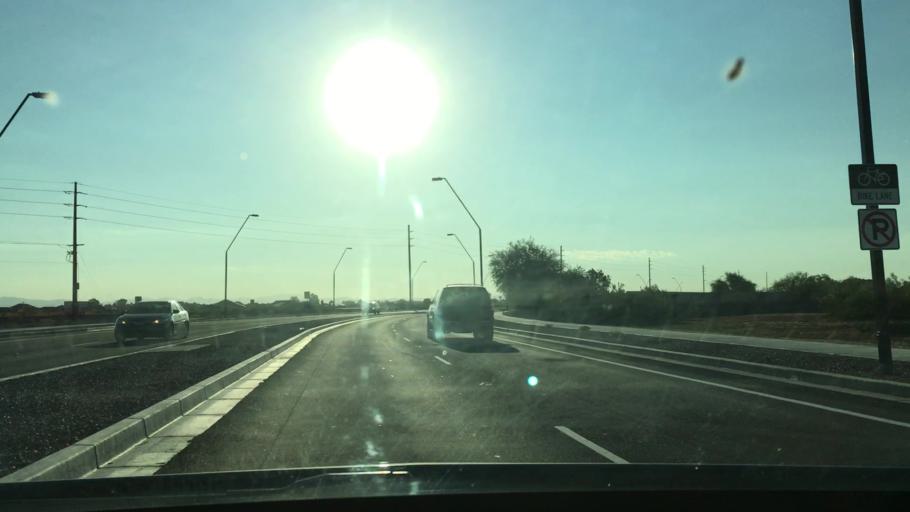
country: US
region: Arizona
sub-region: Maricopa County
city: Queen Creek
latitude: 33.2744
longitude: -111.6659
